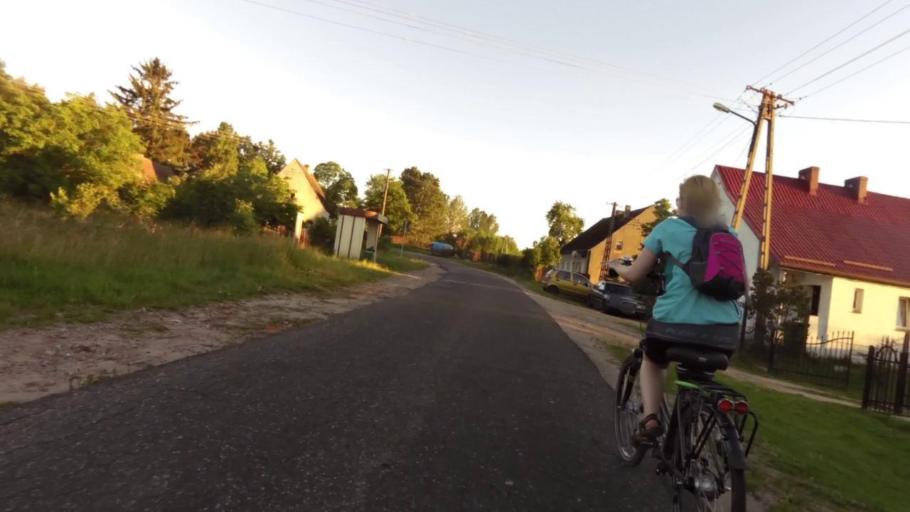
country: PL
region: West Pomeranian Voivodeship
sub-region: Powiat bialogardzki
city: Bialogard
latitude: 54.0412
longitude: 16.0472
